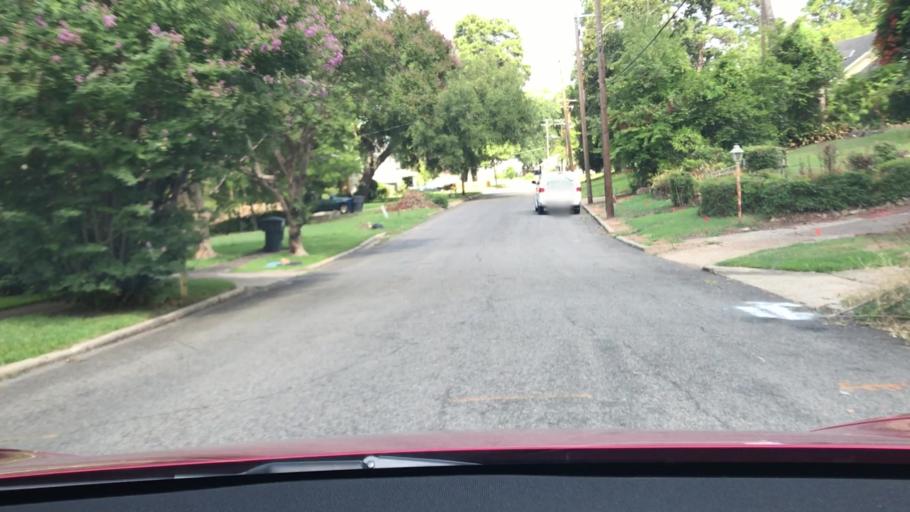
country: US
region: Louisiana
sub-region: Bossier Parish
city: Bossier City
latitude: 32.4807
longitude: -93.7333
